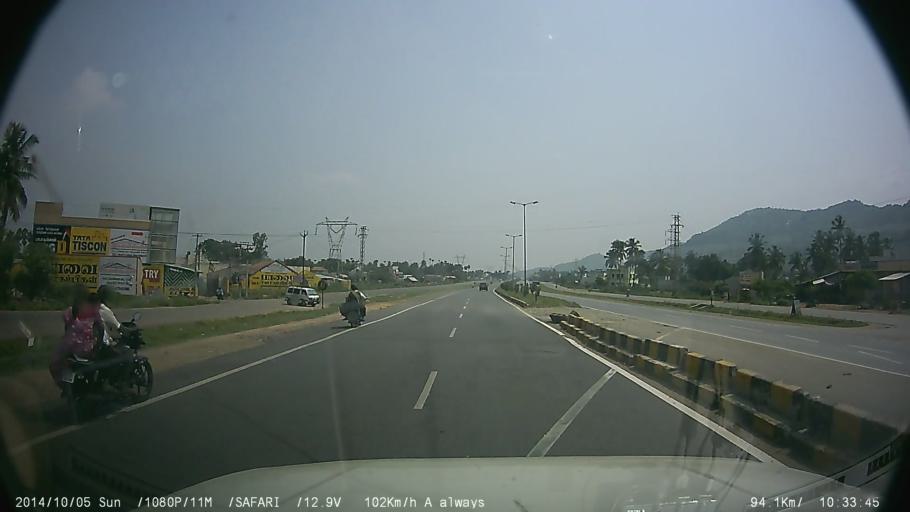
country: IN
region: Tamil Nadu
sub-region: Salem
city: Salem
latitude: 11.6463
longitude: 78.1818
